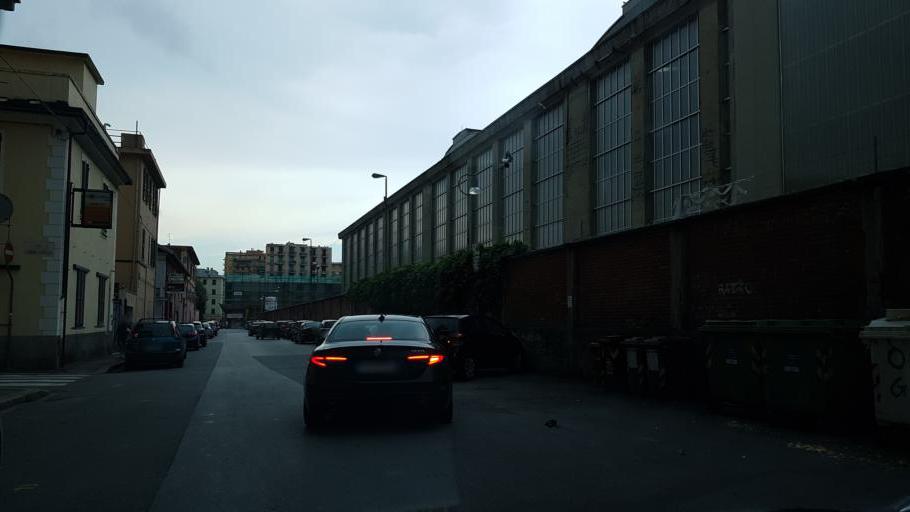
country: IT
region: Liguria
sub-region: Provincia di Genova
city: San Teodoro
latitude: 44.4257
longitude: 8.8408
